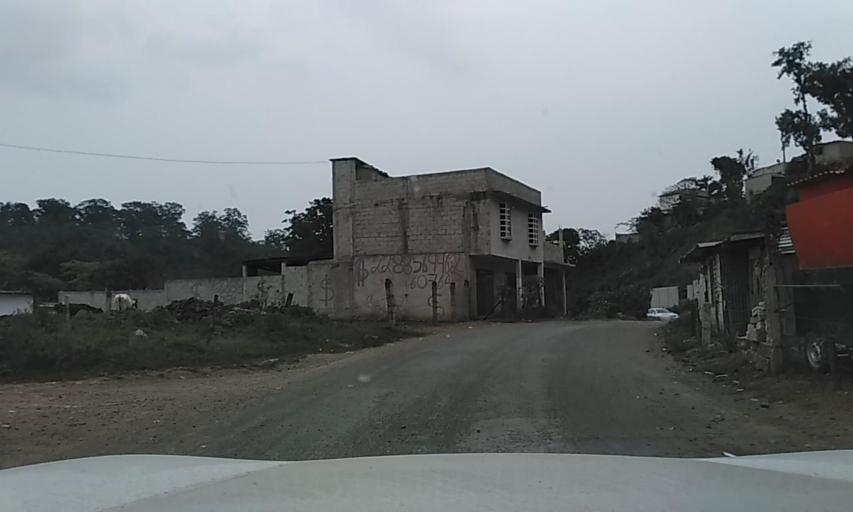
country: MX
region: Veracruz
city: El Castillo
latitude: 19.5714
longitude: -96.8909
